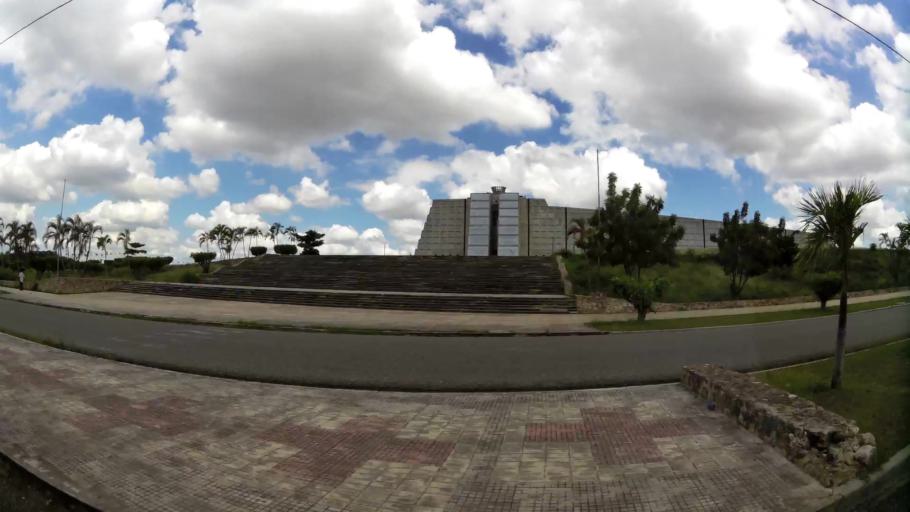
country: DO
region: Santo Domingo
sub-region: Santo Domingo
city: Santo Domingo Este
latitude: 18.4770
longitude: -69.8676
